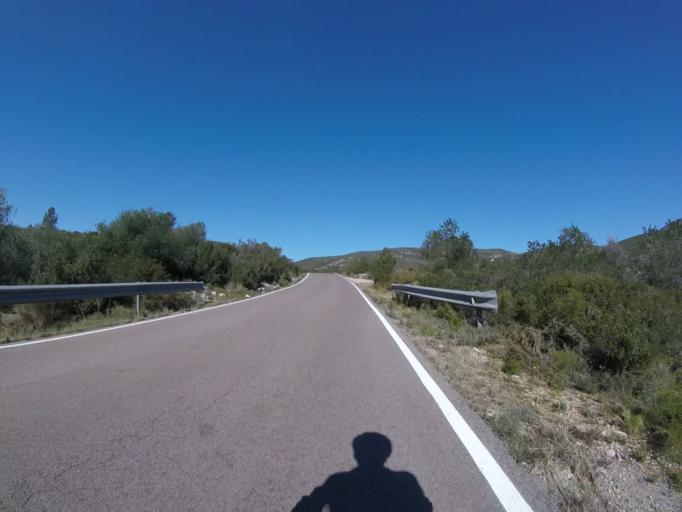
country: ES
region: Valencia
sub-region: Provincia de Castello
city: Santa Magdalena de Pulpis
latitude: 40.3775
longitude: 0.2707
